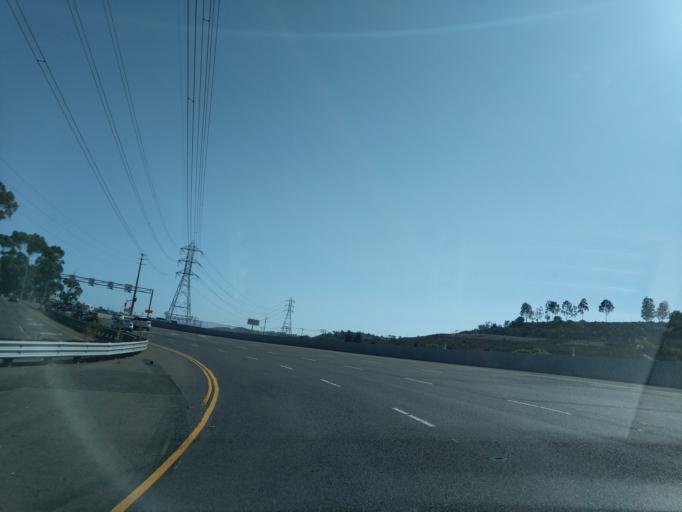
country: US
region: California
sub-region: Orange County
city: Mission Viejo
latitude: 33.5818
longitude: -117.6729
